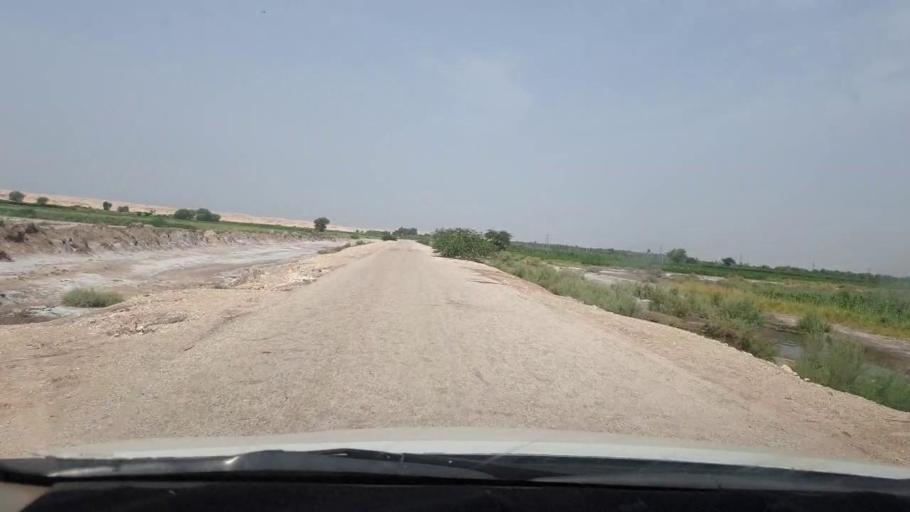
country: PK
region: Sindh
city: Rohri
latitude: 27.5953
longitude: 68.9923
